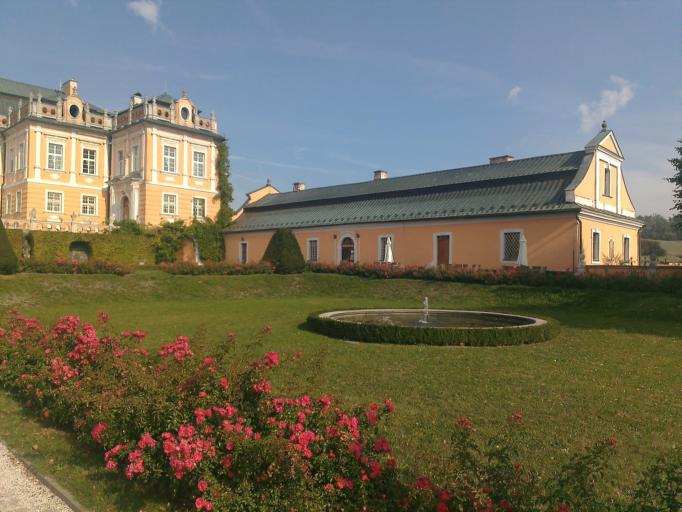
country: CZ
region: Pardubicky
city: Prosec
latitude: 49.8523
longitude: 16.1455
